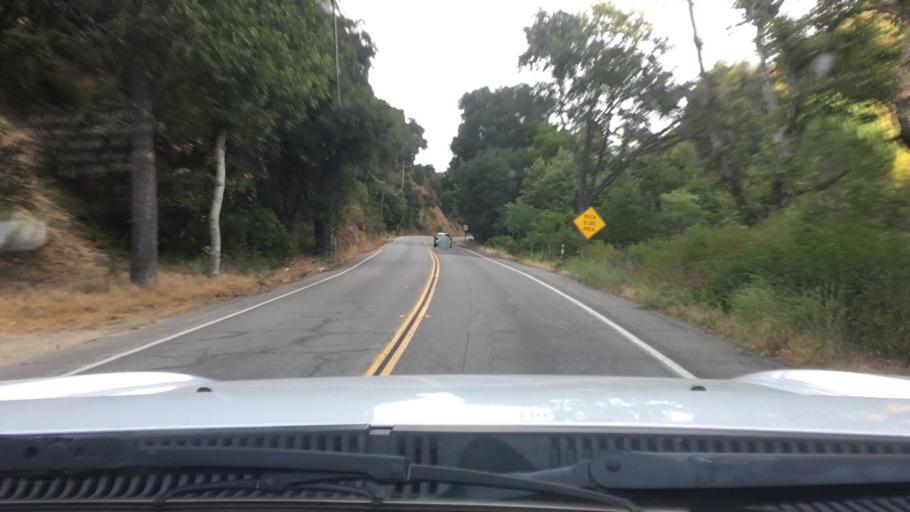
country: US
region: California
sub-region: San Luis Obispo County
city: Atascadero
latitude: 35.4532
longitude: -120.6933
